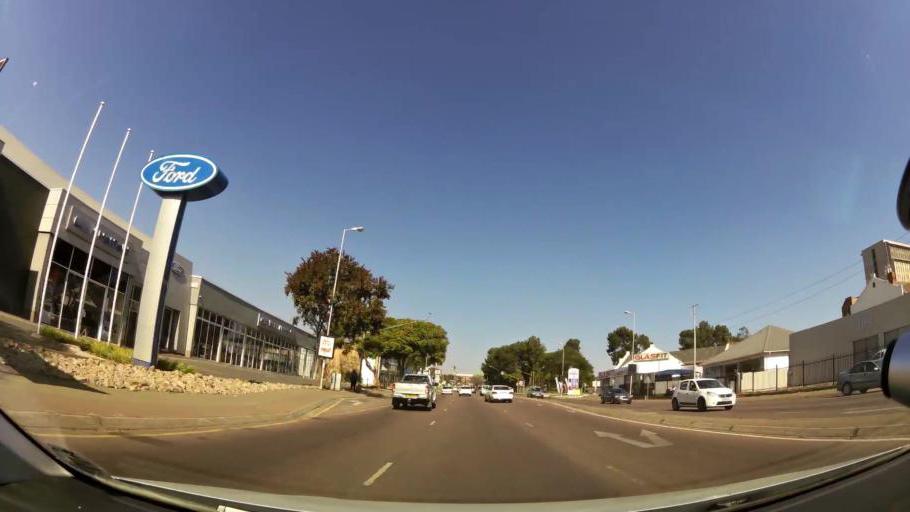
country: ZA
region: Gauteng
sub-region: City of Tshwane Metropolitan Municipality
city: Pretoria
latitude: -25.7491
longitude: 28.2401
